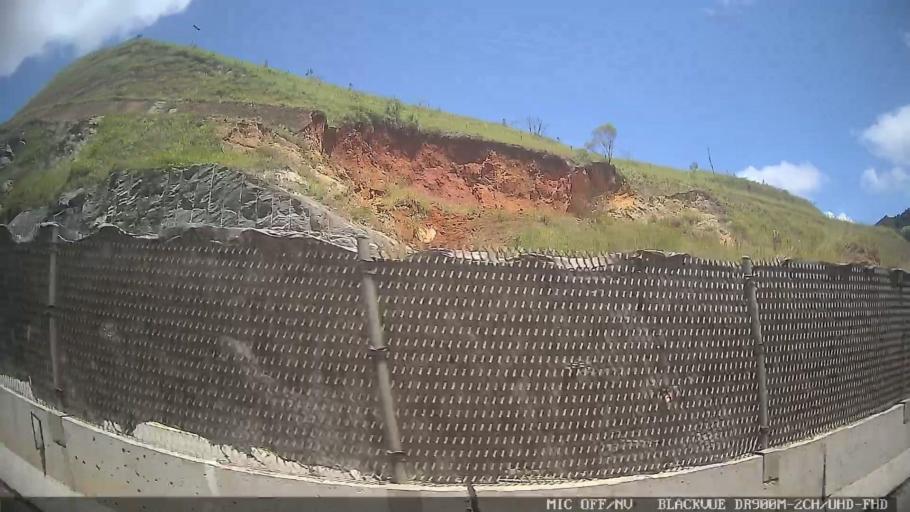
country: BR
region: Sao Paulo
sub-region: Caraguatatuba
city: Caraguatatuba
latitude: -23.5078
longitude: -45.5591
